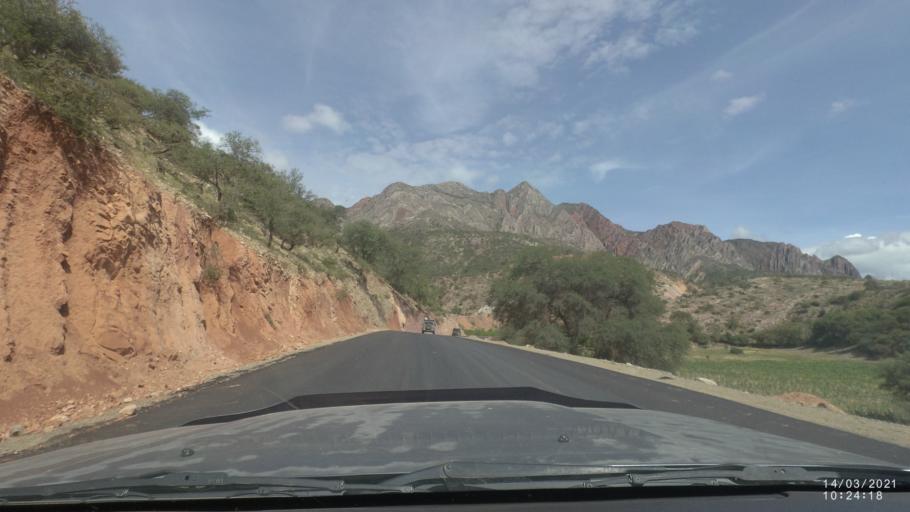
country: BO
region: Cochabamba
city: Cliza
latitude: -17.9148
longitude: -65.8761
